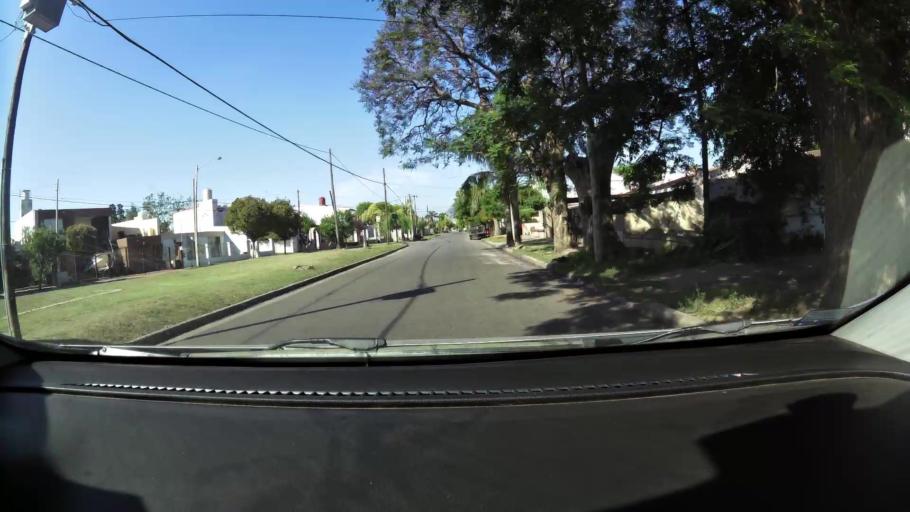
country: AR
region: Cordoba
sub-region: Departamento de Capital
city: Cordoba
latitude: -31.3639
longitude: -64.1897
